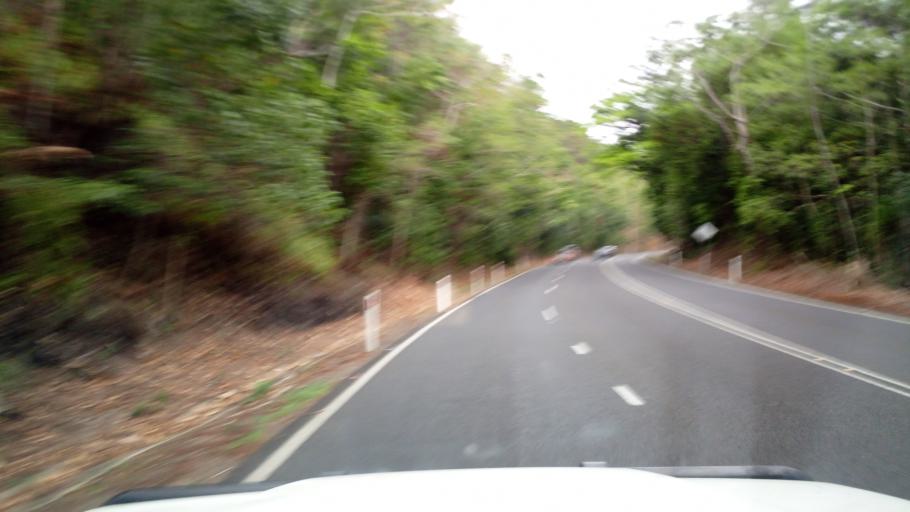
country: AU
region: Queensland
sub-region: Cairns
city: Redlynch
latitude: -16.8507
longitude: 145.6842
